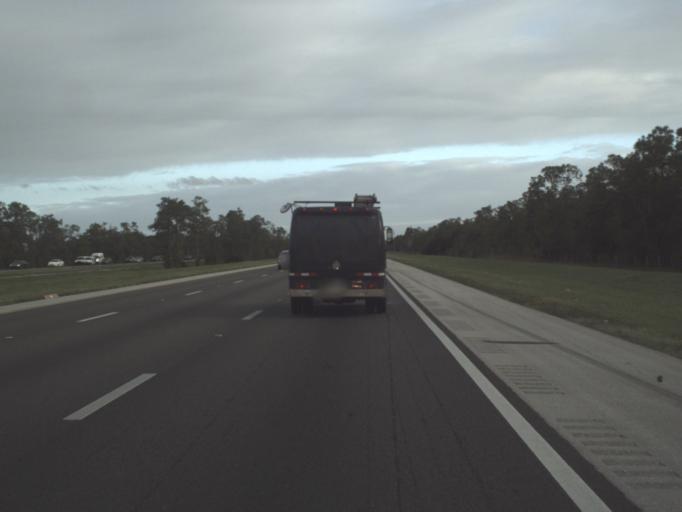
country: US
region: Florida
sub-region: Lee County
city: Estero
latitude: 26.4016
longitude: -81.7726
